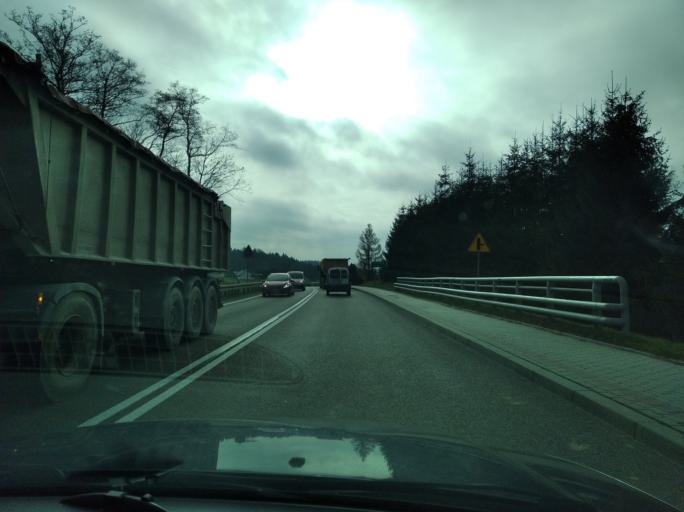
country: PL
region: Subcarpathian Voivodeship
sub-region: Powiat brzozowski
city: Jablonica Polska
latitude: 49.7222
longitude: 21.9009
